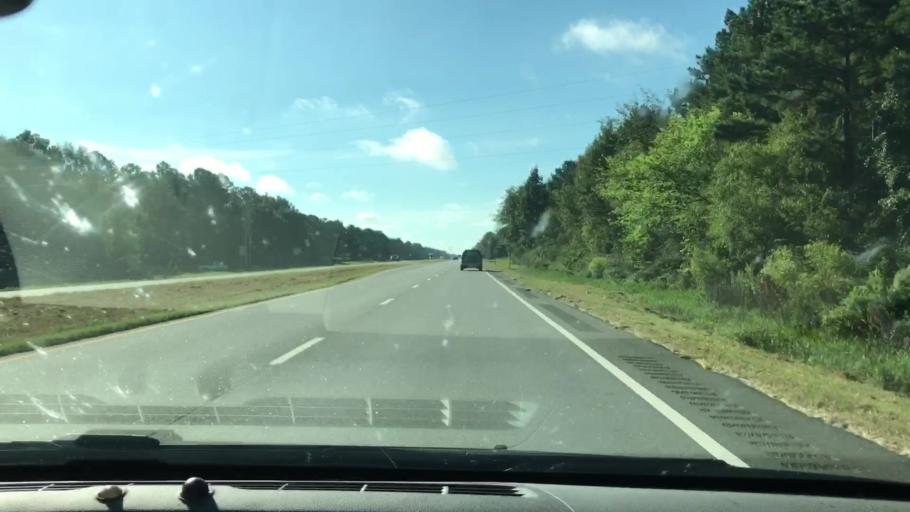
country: US
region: Georgia
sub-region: Lee County
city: Leesburg
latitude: 31.6927
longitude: -84.3148
